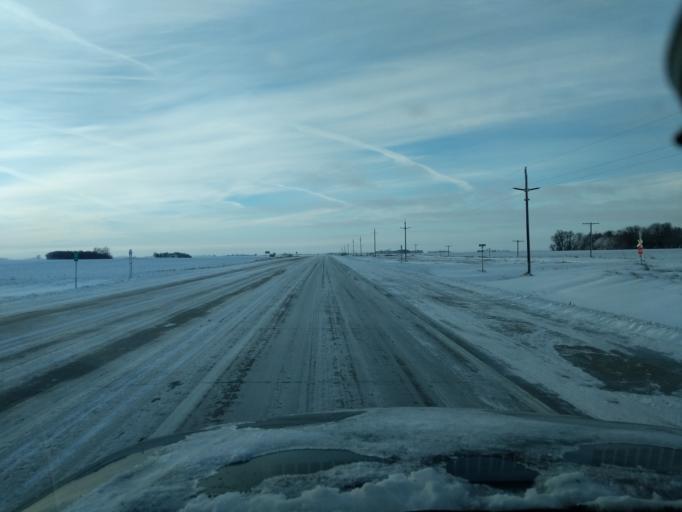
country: US
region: Minnesota
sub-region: Renville County
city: Hector
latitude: 44.7528
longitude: -94.7921
